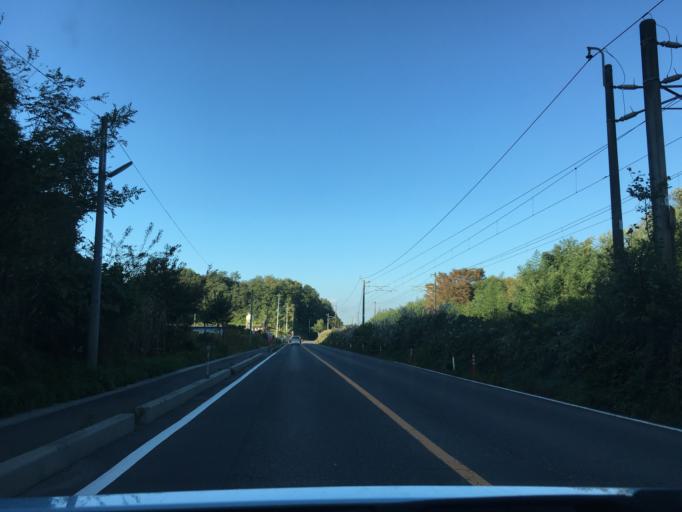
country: JP
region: Fukushima
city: Sukagawa
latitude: 37.3136
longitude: 140.3778
